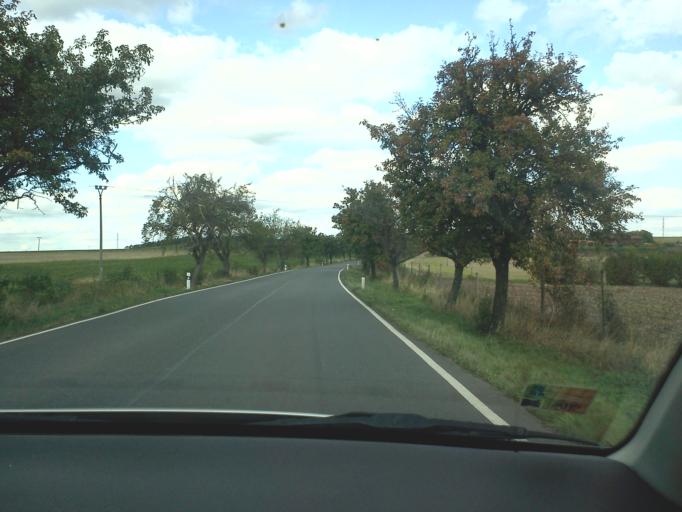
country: CZ
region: Central Bohemia
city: Cesky Brod
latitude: 50.0805
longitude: 14.8649
